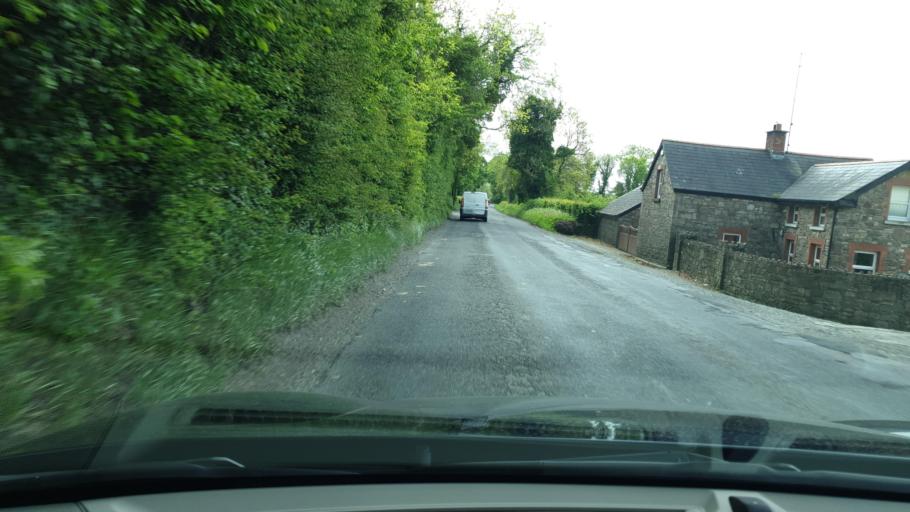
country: IE
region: Ulster
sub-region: An Cabhan
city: Kingscourt
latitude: 53.8395
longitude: -6.7690
